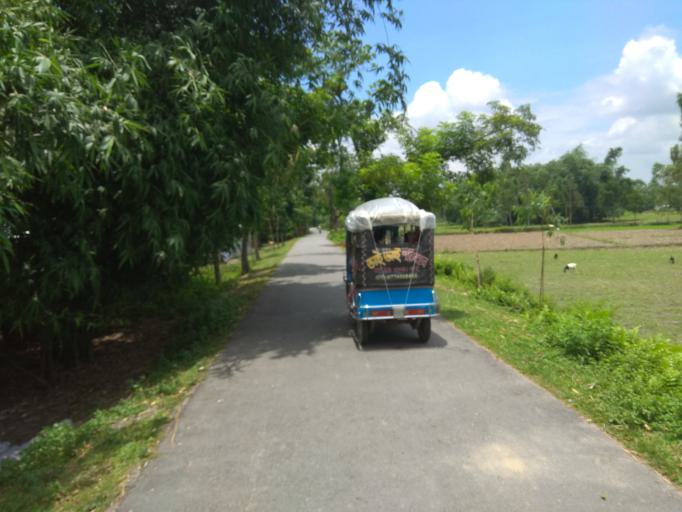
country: IN
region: West Bengal
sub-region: Koch Bihar
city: Haldibari
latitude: 26.2316
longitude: 88.8878
